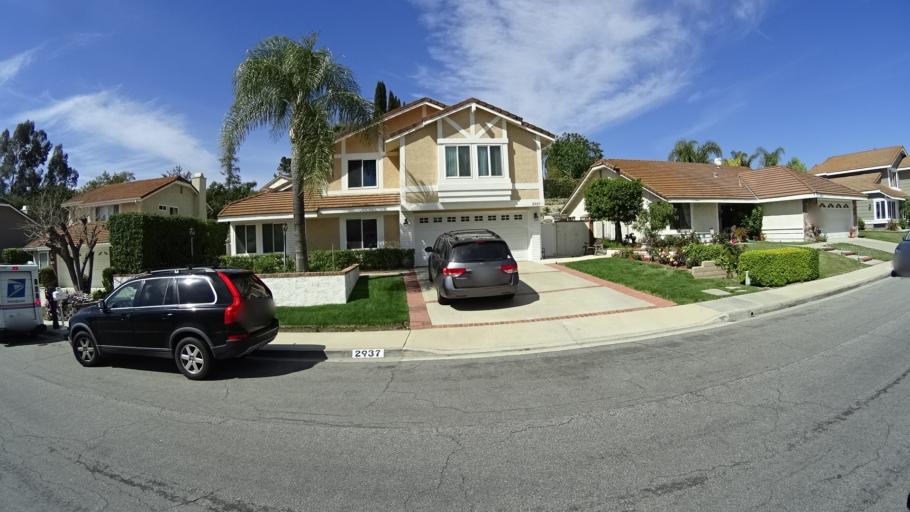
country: US
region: California
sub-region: Ventura County
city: Thousand Oaks
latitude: 34.2189
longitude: -118.8381
